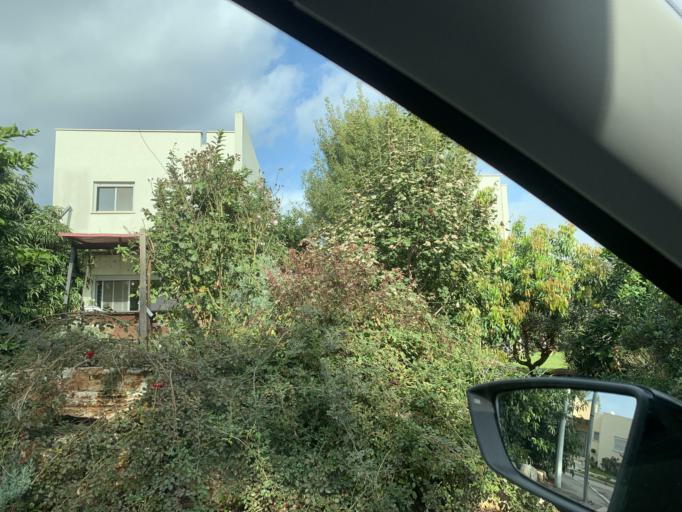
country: PS
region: West Bank
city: Qalqilyah
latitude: 32.1997
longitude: 34.9491
